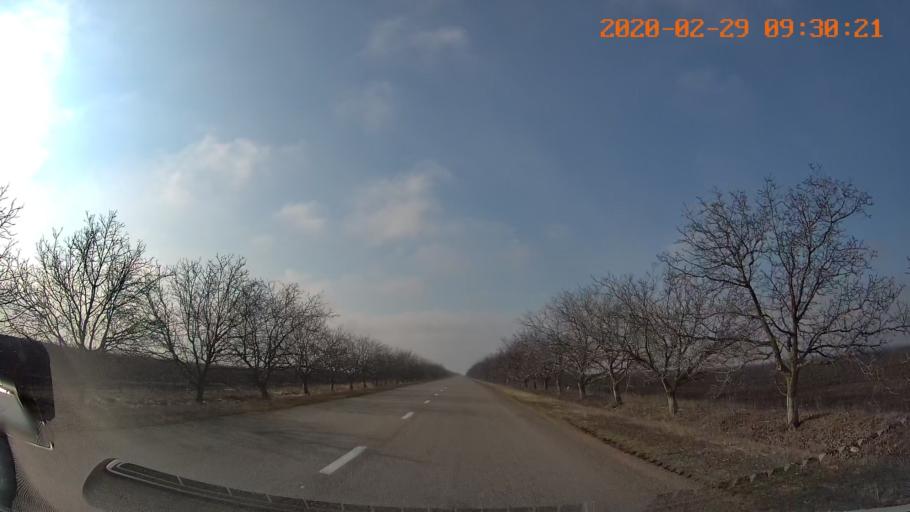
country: MD
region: Telenesti
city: Dnestrovsc
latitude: 46.6676
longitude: 29.9170
